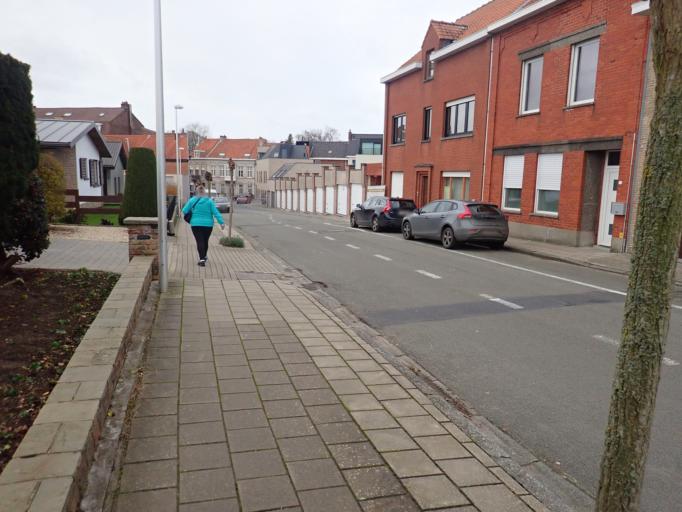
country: BE
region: Flanders
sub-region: Provincie West-Vlaanderen
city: Ieper
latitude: 50.8520
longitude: 2.8941
